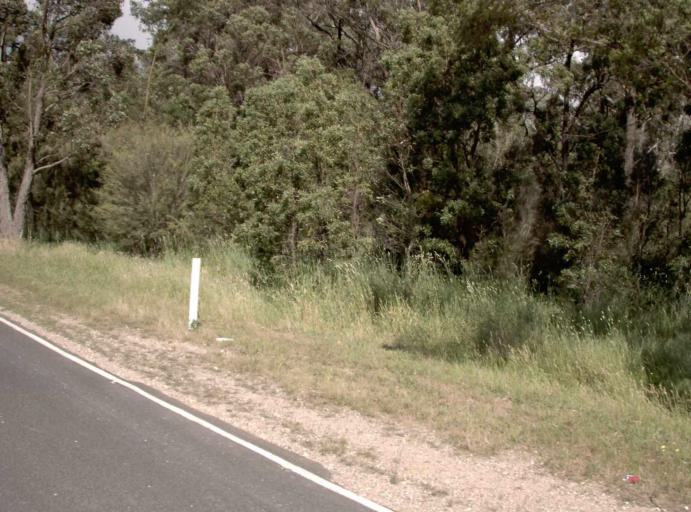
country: AU
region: Victoria
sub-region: Latrobe
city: Traralgon
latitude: -38.1354
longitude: 146.5448
